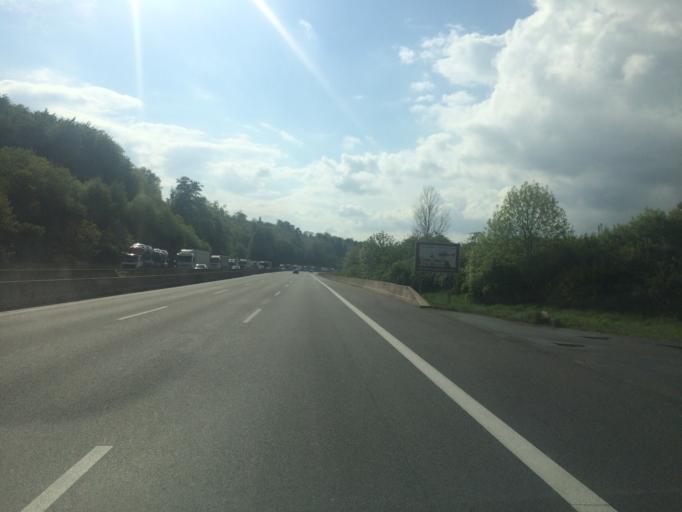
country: DE
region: Lower Saxony
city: Buchholz
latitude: 52.2159
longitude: 9.1747
